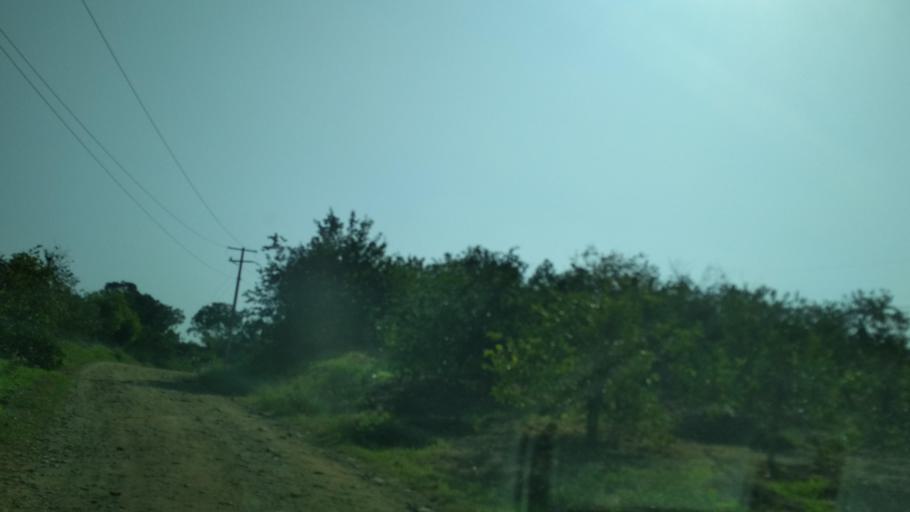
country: MX
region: Puebla
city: San Jose Acateno
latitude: 20.1714
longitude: -97.1747
